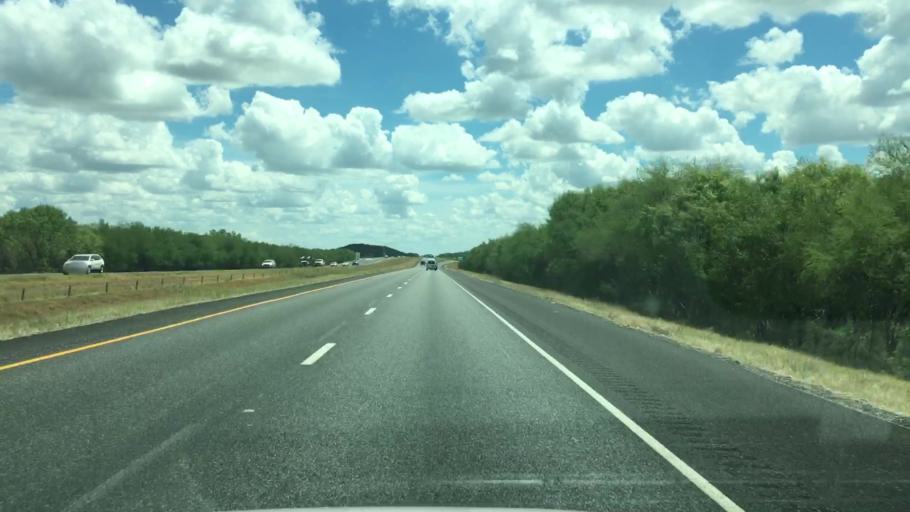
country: US
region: Texas
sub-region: Atascosa County
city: Pleasanton
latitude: 28.7415
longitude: -98.2921
